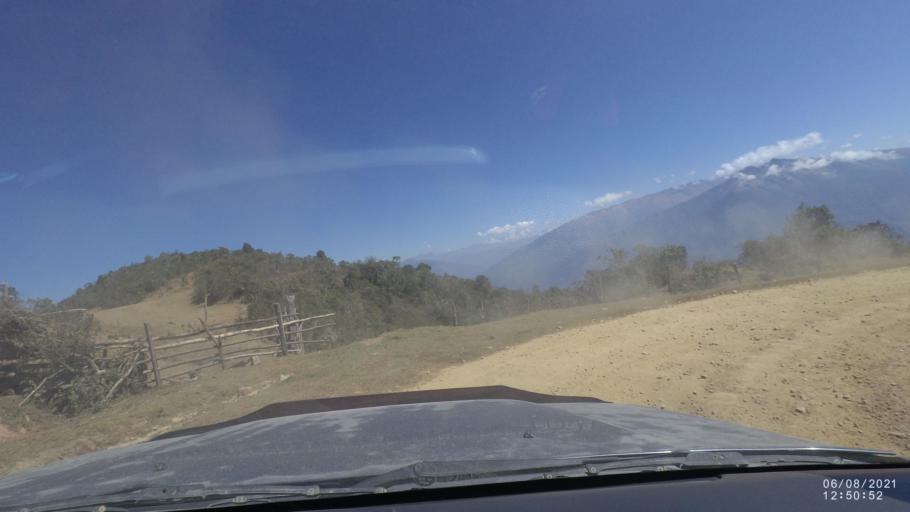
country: BO
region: Cochabamba
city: Colchani
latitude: -16.7616
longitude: -66.6792
